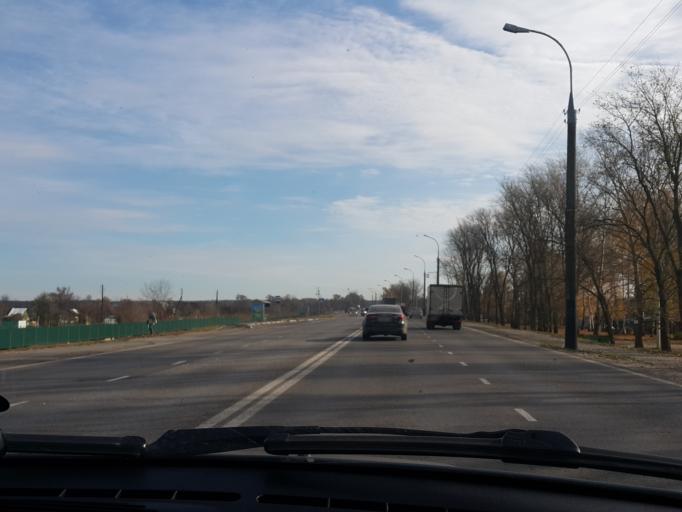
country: RU
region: Tambov
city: Tambov
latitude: 52.7211
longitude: 41.4898
